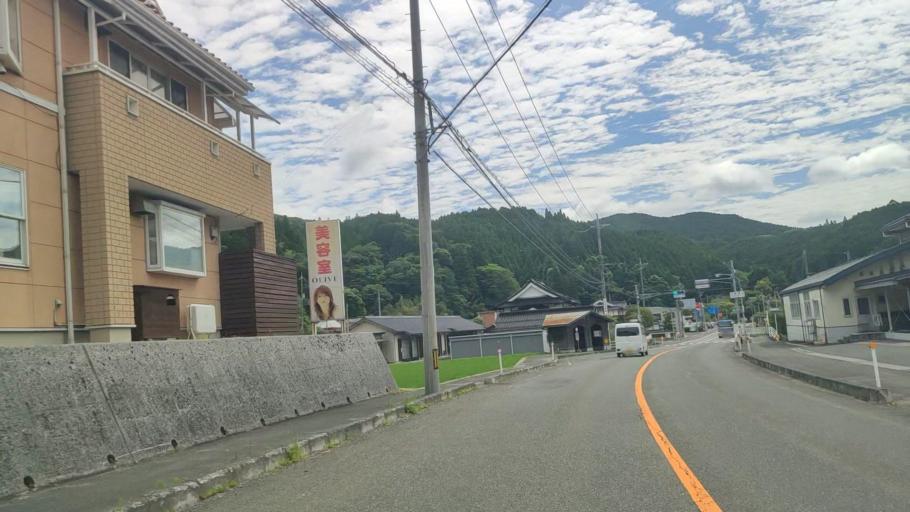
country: JP
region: Okayama
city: Niimi
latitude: 35.1573
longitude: 133.6212
